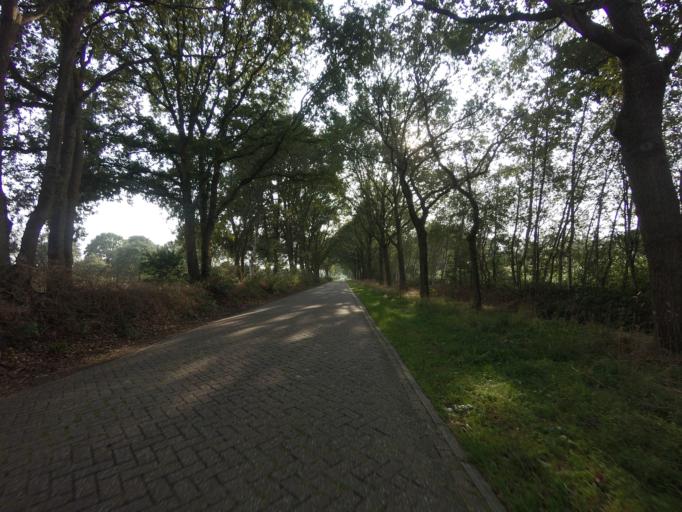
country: NL
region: Drenthe
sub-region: Gemeente Tynaarlo
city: Vries
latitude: 53.1211
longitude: 6.5537
